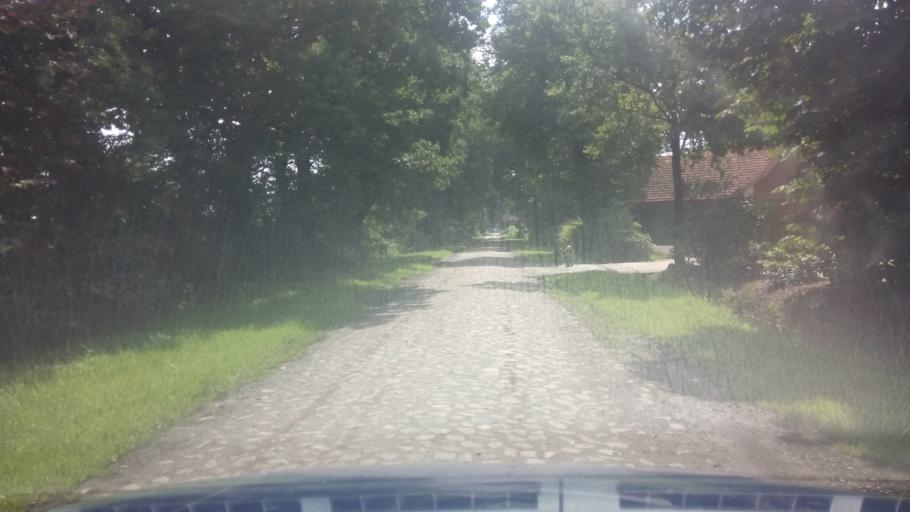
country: DE
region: Lower Saxony
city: Osterholz-Scharmbeck
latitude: 53.2359
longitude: 8.7475
